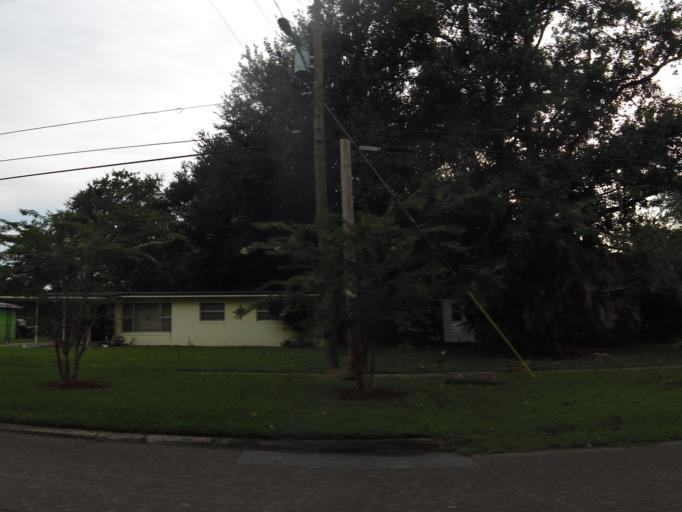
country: US
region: Florida
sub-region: Duval County
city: Jacksonville
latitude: 30.4013
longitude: -81.7199
